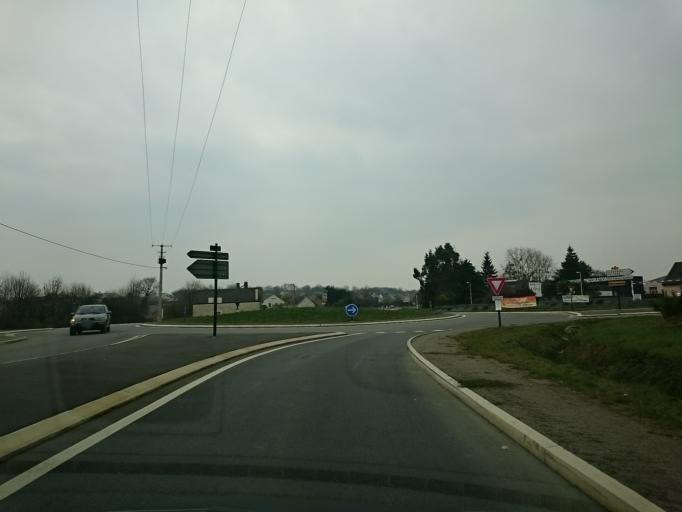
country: FR
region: Brittany
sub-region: Departement d'Ille-et-Vilaine
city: Bain-de-Bretagne
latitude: 47.8539
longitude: -1.6790
